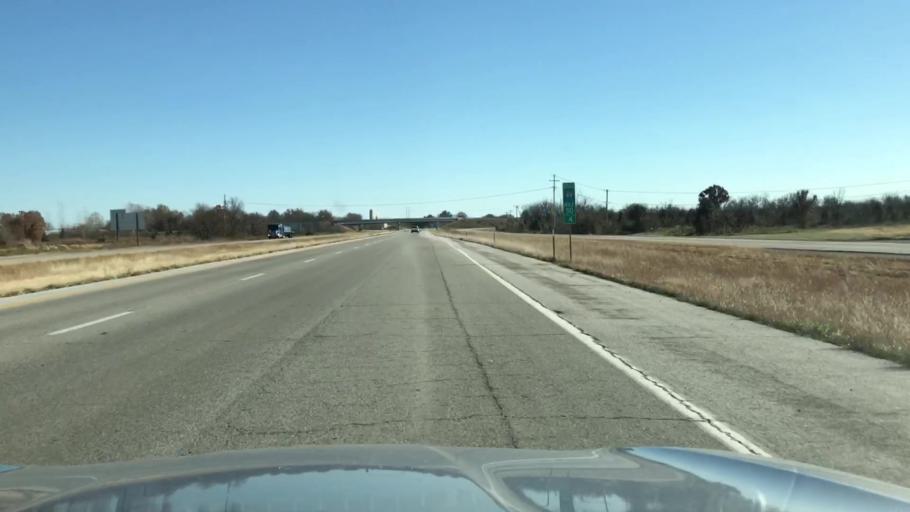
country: US
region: Missouri
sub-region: Jasper County
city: Carthage
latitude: 37.1368
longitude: -94.3188
